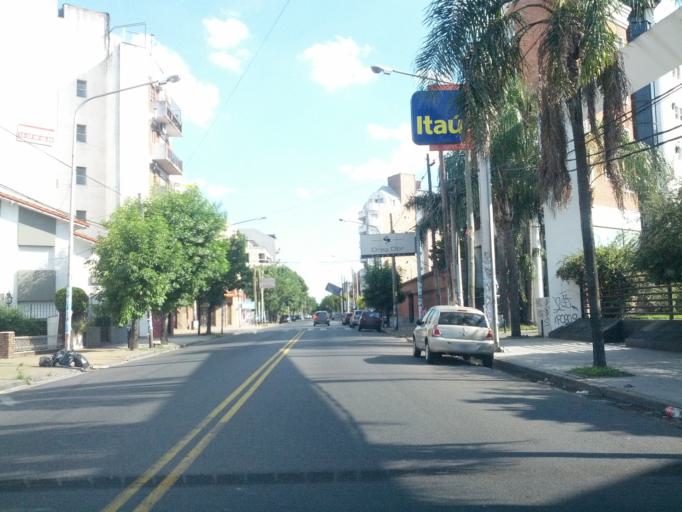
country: AR
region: Buenos Aires
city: San Justo
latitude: -34.6514
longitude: -58.5635
